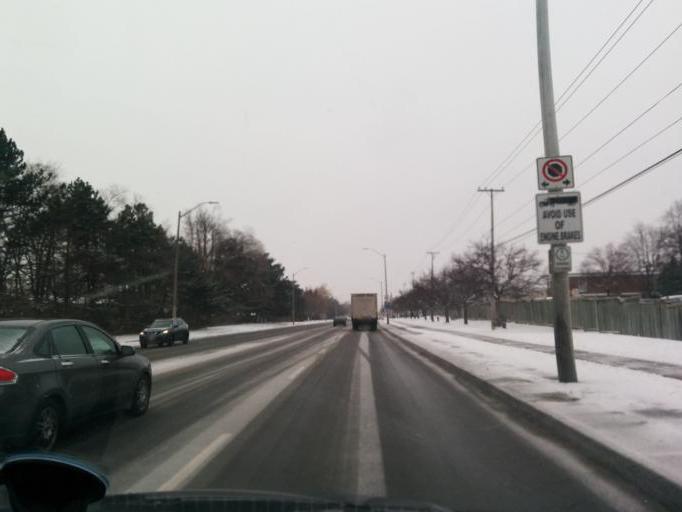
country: CA
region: Ontario
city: Mississauga
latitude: 43.5165
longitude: -79.6371
